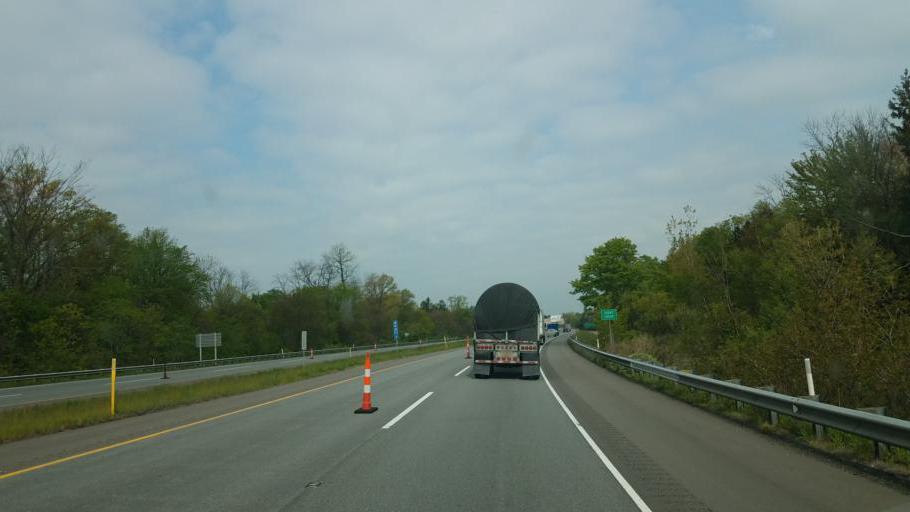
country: US
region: Indiana
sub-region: Saint Joseph County
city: Georgetown
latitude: 41.7178
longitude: -86.2408
